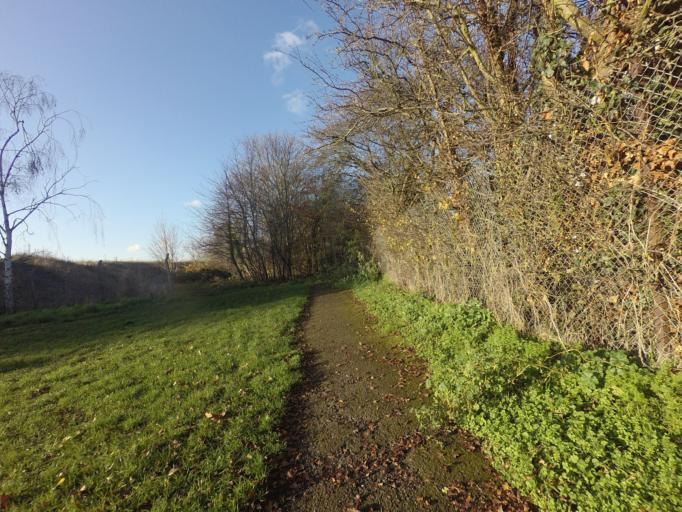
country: GB
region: England
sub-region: Greater London
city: Feltham
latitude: 51.4524
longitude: -0.4107
